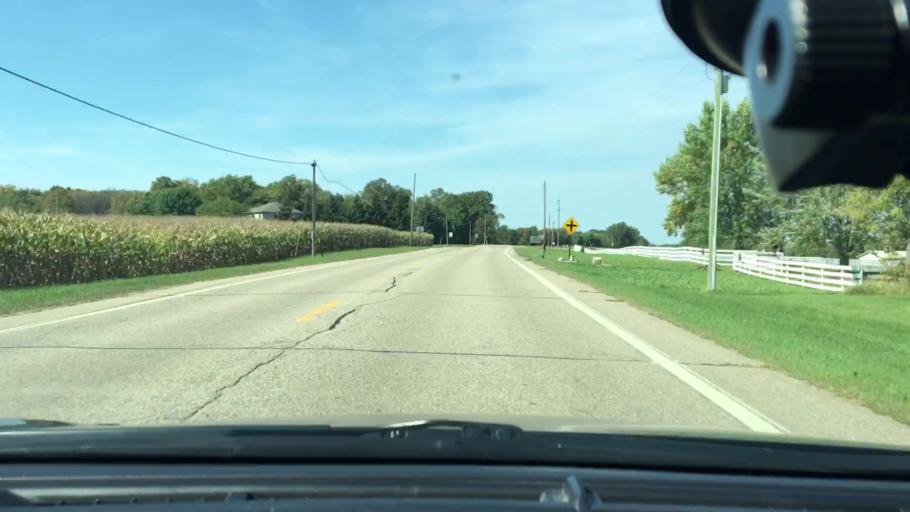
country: US
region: Minnesota
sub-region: Hennepin County
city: Corcoran
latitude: 45.1134
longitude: -93.5817
